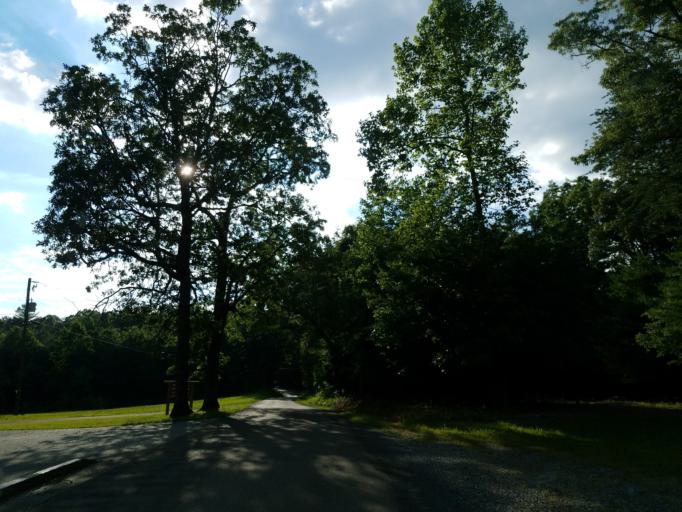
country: US
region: Georgia
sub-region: Gilmer County
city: Ellijay
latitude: 34.6534
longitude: -84.2924
